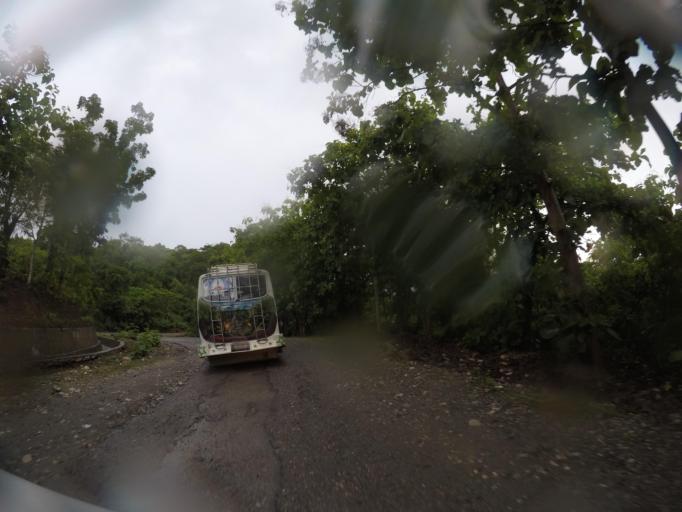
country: ID
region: East Nusa Tenggara
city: Atambua
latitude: -8.9622
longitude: 125.0247
